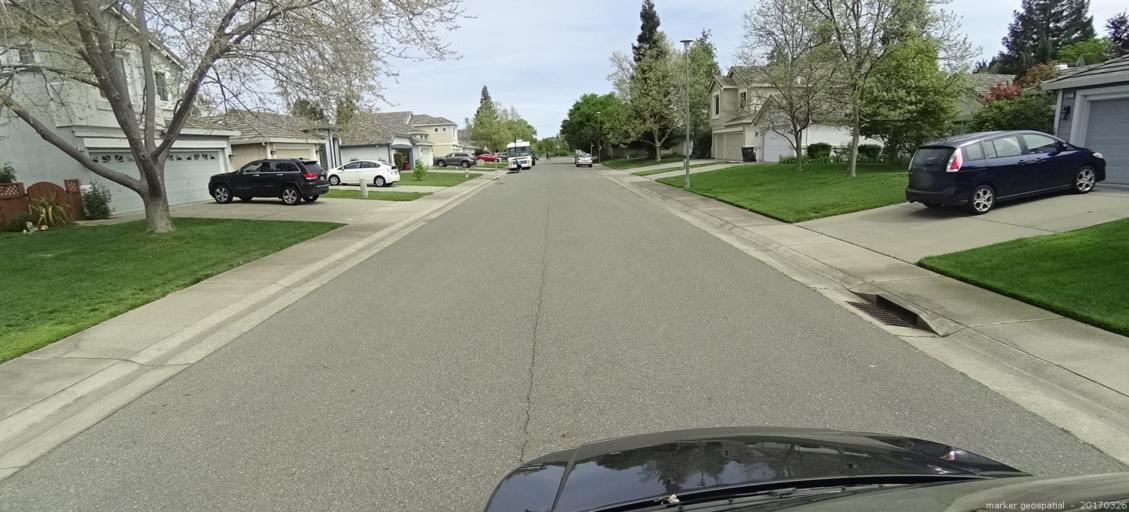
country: US
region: California
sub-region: Sacramento County
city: Laguna
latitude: 38.4394
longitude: -121.4314
